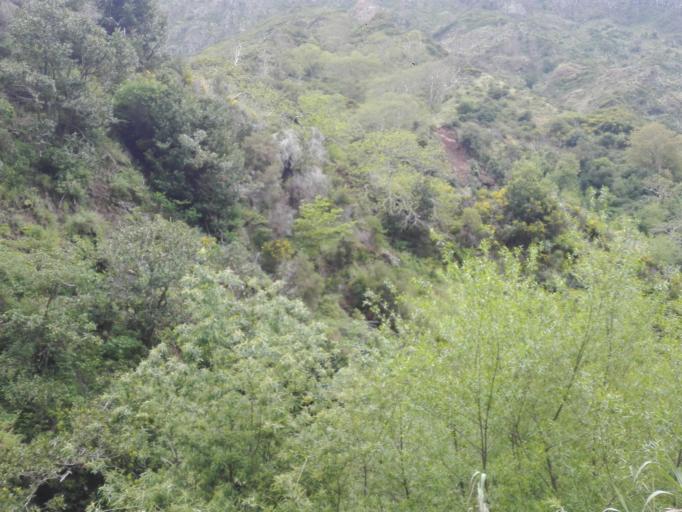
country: PT
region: Madeira
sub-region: Camara de Lobos
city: Curral das Freiras
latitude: 32.7477
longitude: -16.9568
